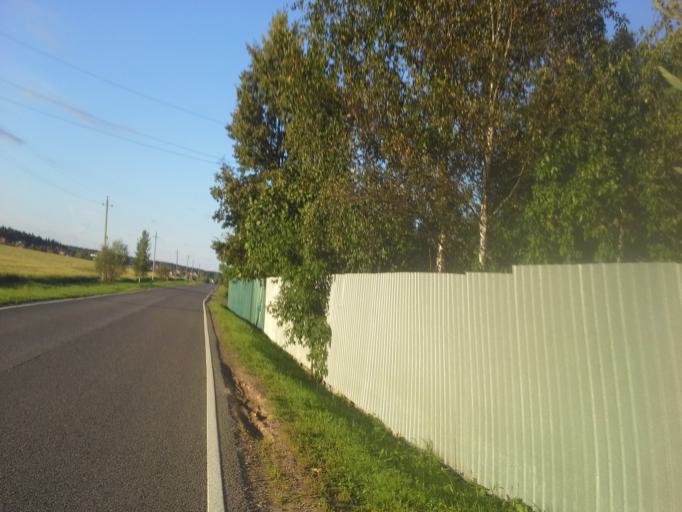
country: RU
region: Moskovskaya
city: Kievskij
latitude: 55.4648
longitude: 36.8909
